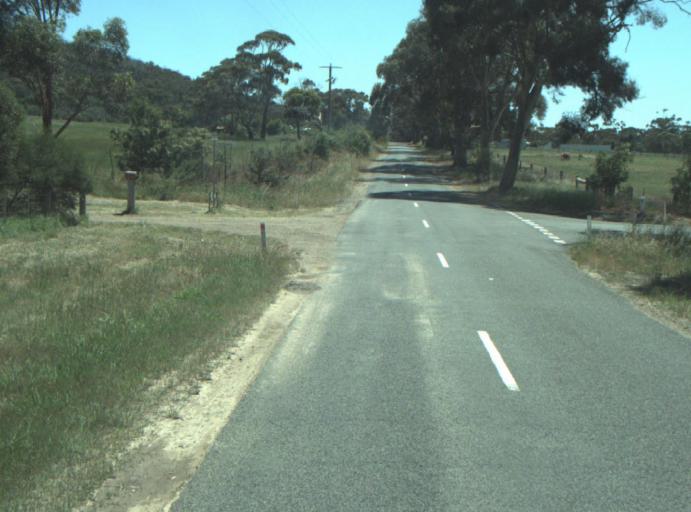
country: AU
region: Victoria
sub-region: Greater Geelong
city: Lara
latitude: -37.8491
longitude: 144.2818
